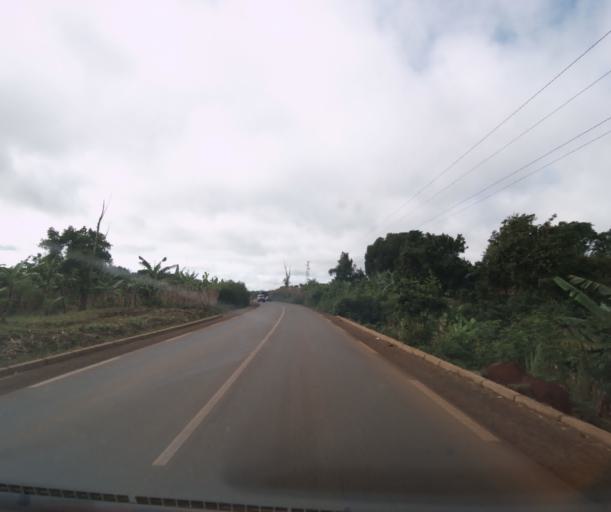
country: CM
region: West
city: Bansoa
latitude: 5.5221
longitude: 10.3420
